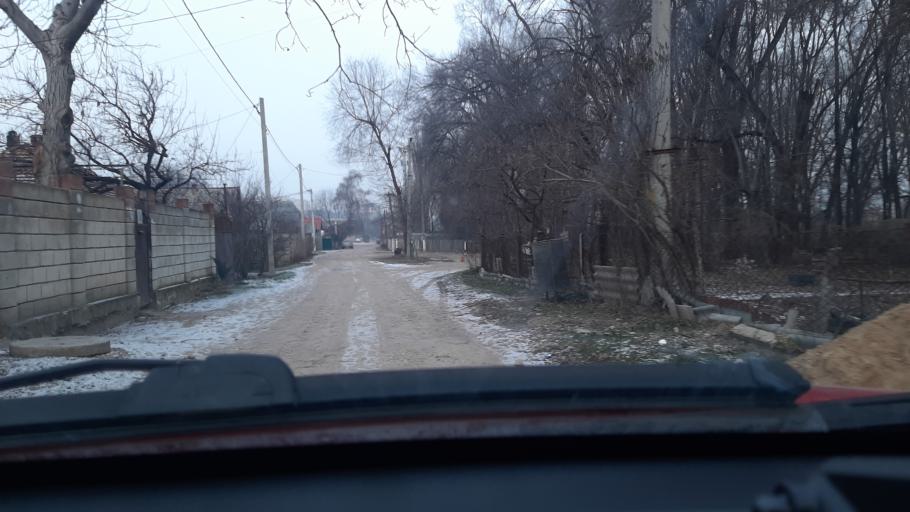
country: MD
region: Chisinau
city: Chisinau
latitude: 46.9873
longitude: 28.8934
